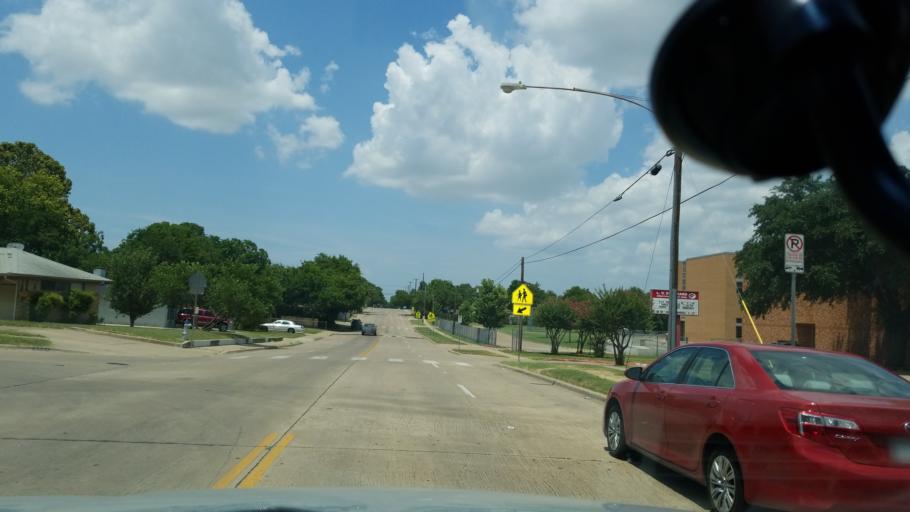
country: US
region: Texas
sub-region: Dallas County
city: Cockrell Hill
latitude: 32.7222
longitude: -96.8689
